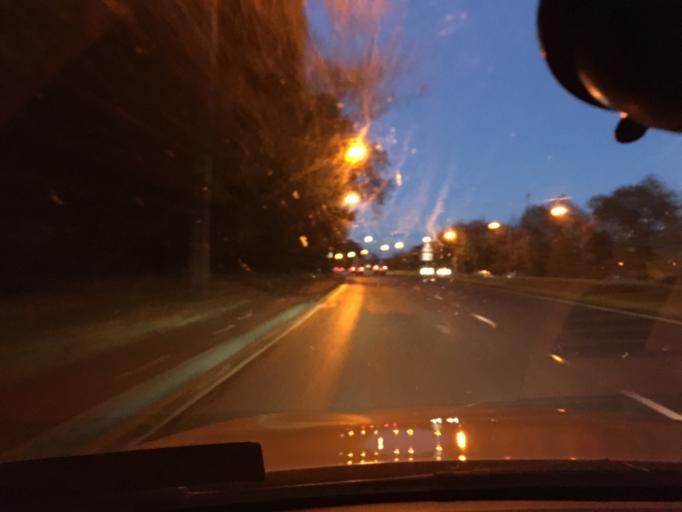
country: GB
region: Northern Ireland
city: Hillsborough
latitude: 54.4751
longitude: -6.0743
